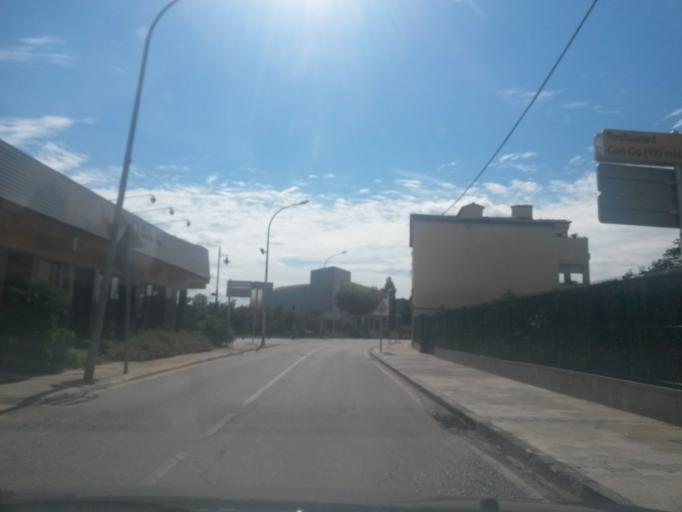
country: ES
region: Catalonia
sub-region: Provincia de Girona
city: la Cellera de Ter
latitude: 41.9688
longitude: 2.6232
